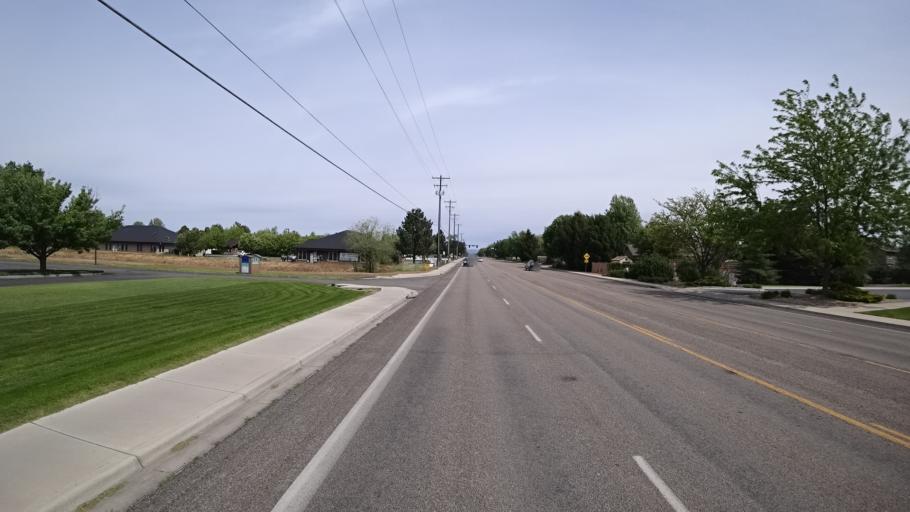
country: US
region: Idaho
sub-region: Ada County
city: Meridian
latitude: 43.5788
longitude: -116.3143
